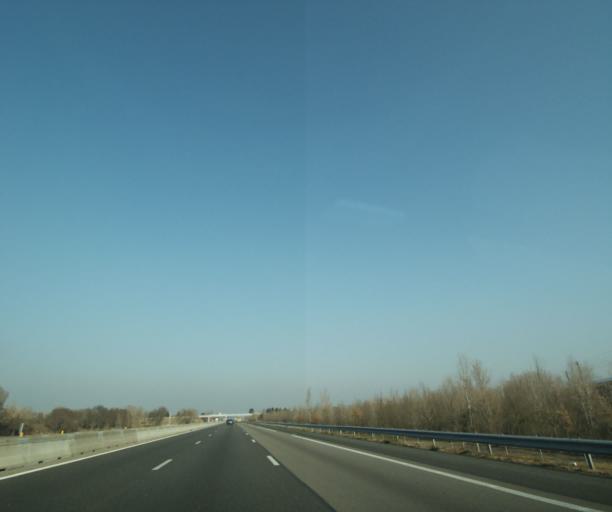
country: FR
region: Rhone-Alpes
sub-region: Departement de la Drome
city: Pierrelatte
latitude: 44.3790
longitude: 4.7322
